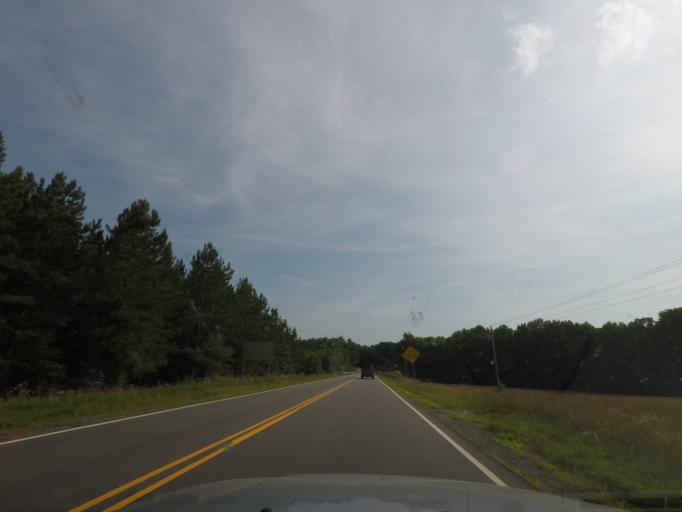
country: US
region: Virginia
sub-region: Mecklenburg County
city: Chase City
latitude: 36.8199
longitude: -78.5968
